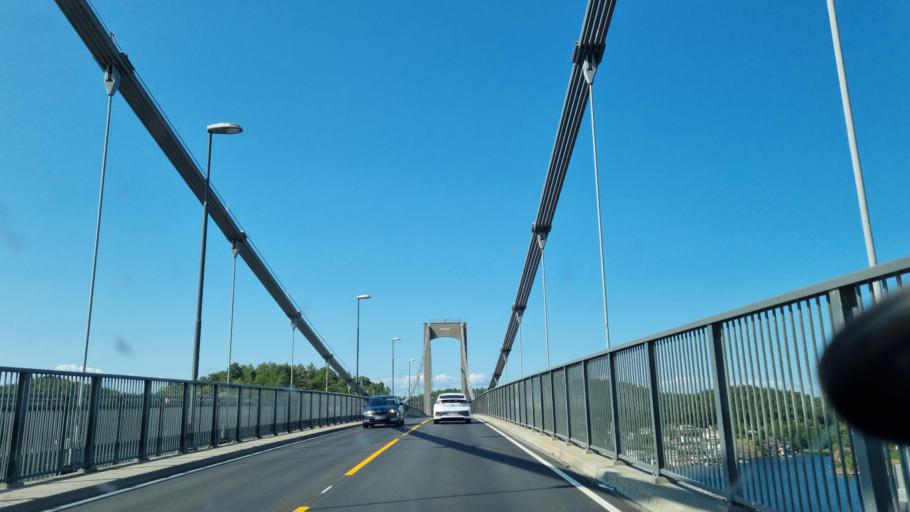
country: NO
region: Aust-Agder
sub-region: Arendal
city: Arendal
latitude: 58.4704
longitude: 8.8232
